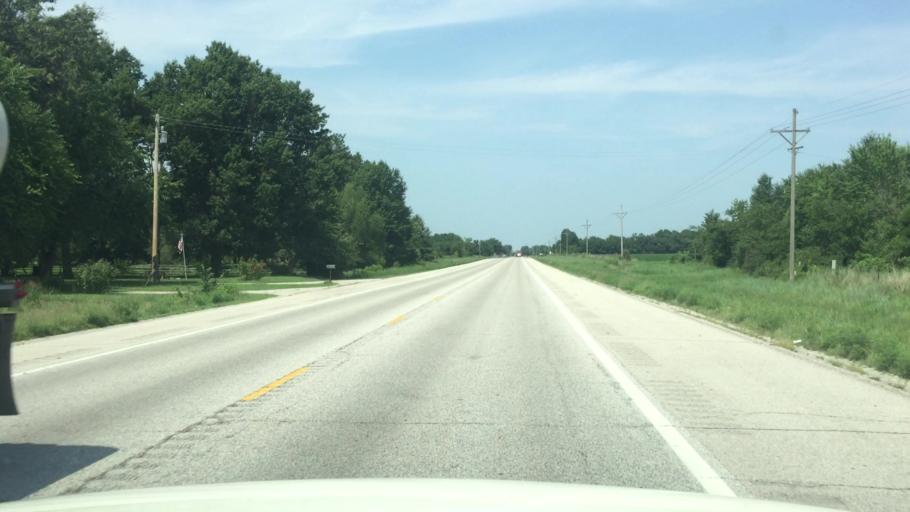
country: US
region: Kansas
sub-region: Cherokee County
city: Galena
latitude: 37.1520
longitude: -94.7043
